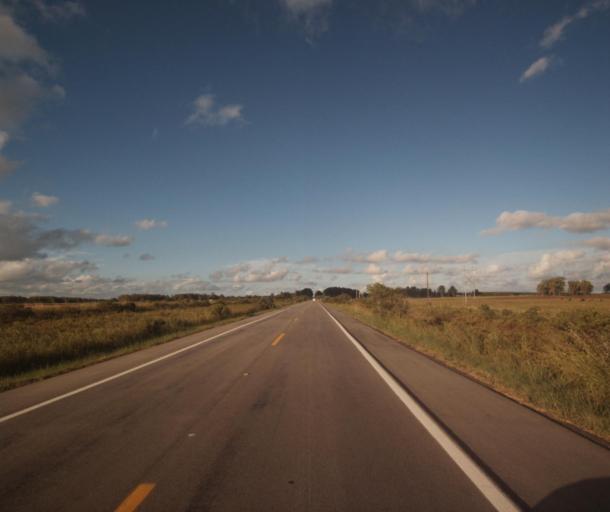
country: BR
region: Rio Grande do Sul
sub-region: Rio Grande
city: Rio Grande
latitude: -32.1305
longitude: -52.3700
